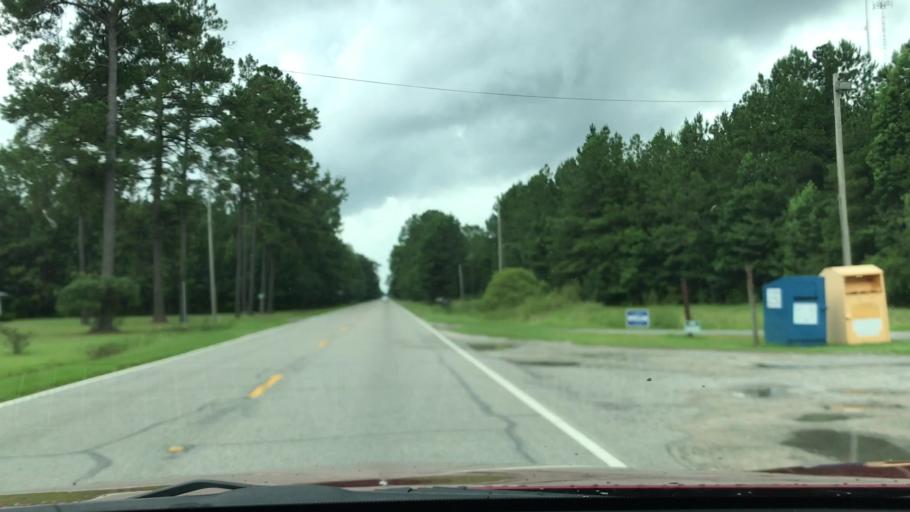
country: US
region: South Carolina
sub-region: Georgetown County
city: Murrells Inlet
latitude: 33.5529
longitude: -79.2187
